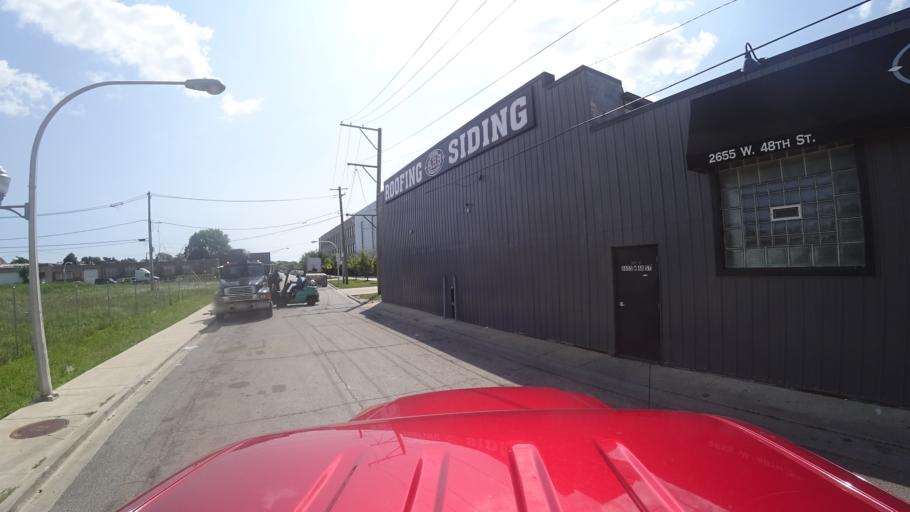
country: US
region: Illinois
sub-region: Cook County
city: Chicago
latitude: 41.8066
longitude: -87.6917
